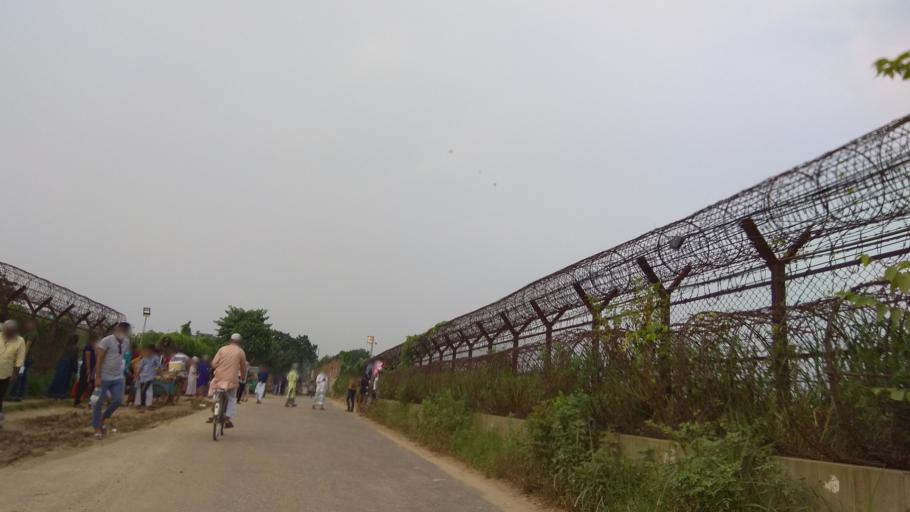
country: BD
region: Dhaka
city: Tungi
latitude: 23.8574
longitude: 90.3864
